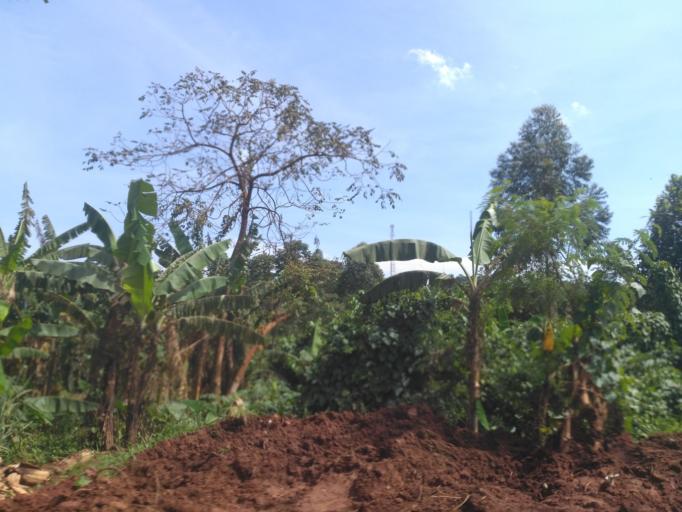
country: UG
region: Central Region
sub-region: Wakiso District
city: Kireka
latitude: 0.4452
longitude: 32.5828
